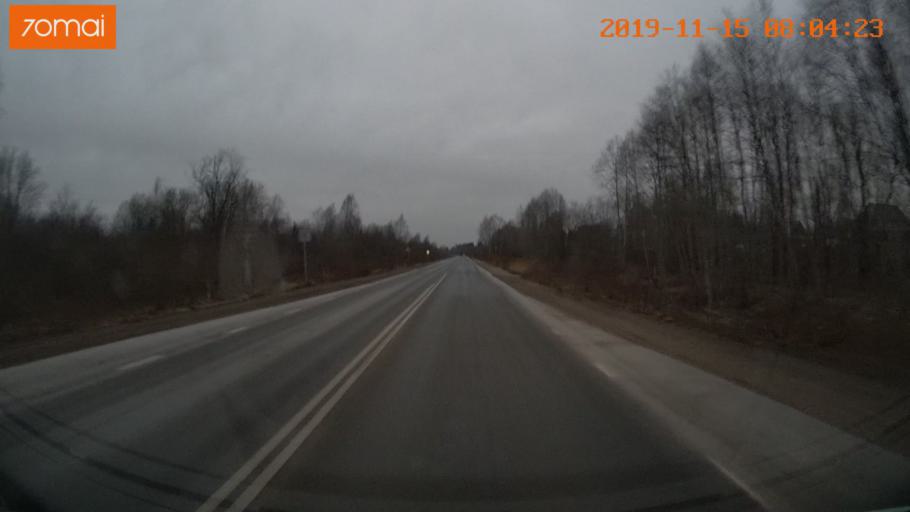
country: RU
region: Vologda
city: Cherepovets
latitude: 59.0077
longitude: 38.0769
